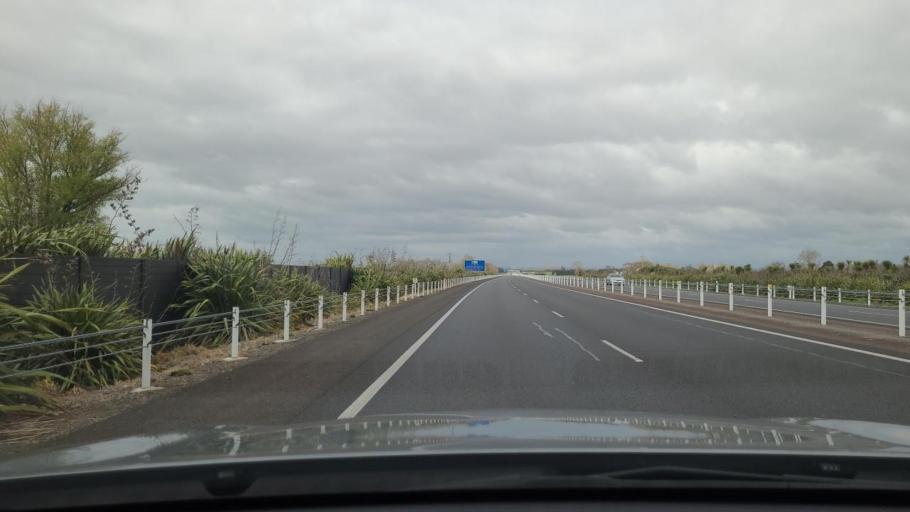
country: NZ
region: Bay of Plenty
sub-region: Western Bay of Plenty District
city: Maketu
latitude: -37.7620
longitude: 176.3700
